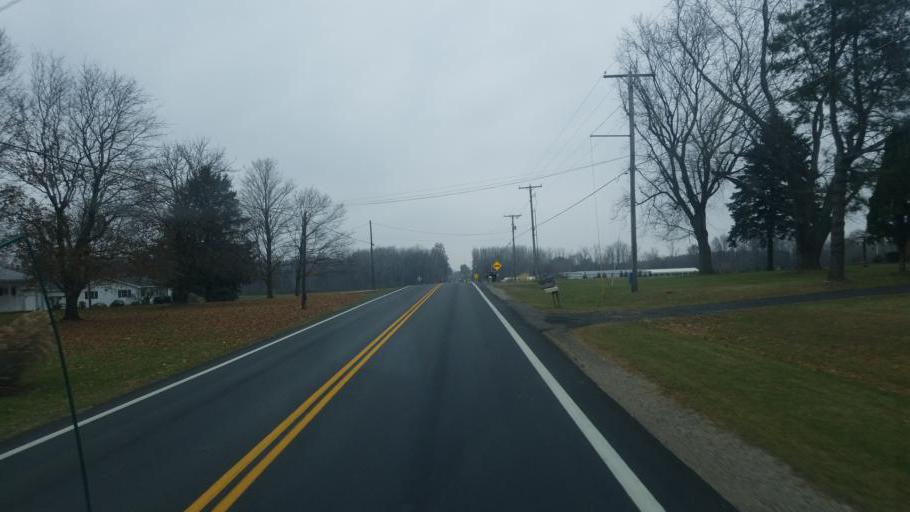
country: US
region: Ohio
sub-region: Crawford County
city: Galion
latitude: 40.7791
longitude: -82.7906
